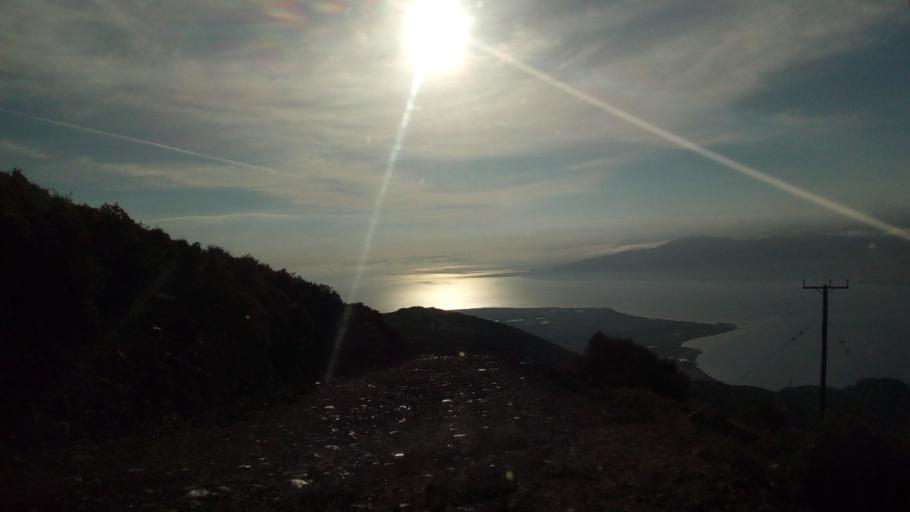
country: GR
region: West Greece
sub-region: Nomos Aitolias kai Akarnanias
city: Nafpaktos
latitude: 38.4167
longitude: 21.8105
